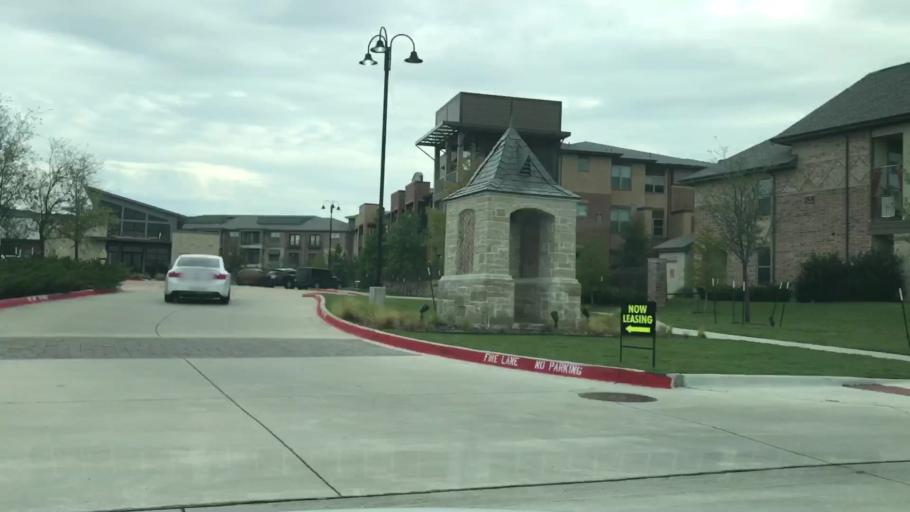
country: US
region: Texas
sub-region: Collin County
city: Frisco
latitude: 33.1276
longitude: -96.8164
